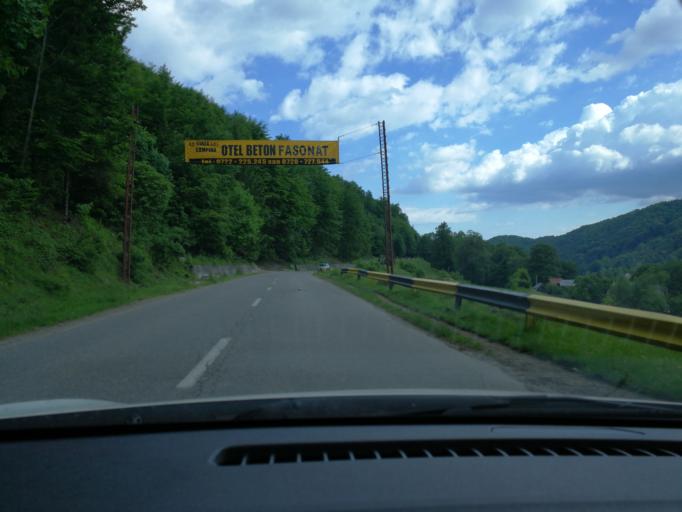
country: RO
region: Prahova
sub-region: Comuna Valea Doftanei
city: Tesila
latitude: 45.2737
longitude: 25.7321
